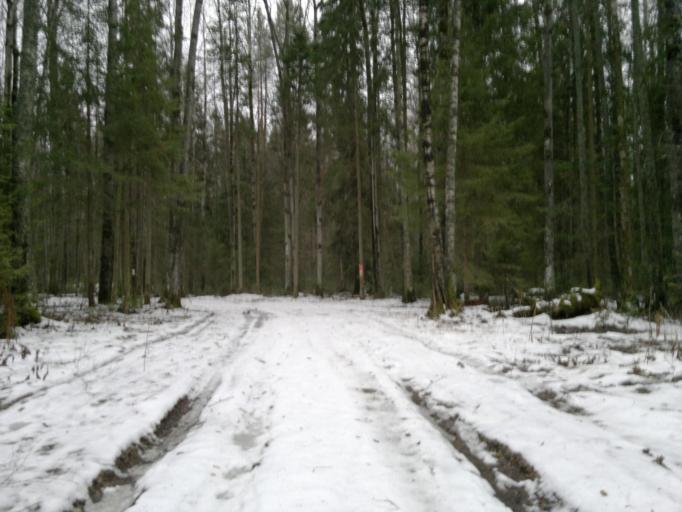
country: RU
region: Mariy-El
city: Yoshkar-Ola
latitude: 56.5942
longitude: 47.9685
